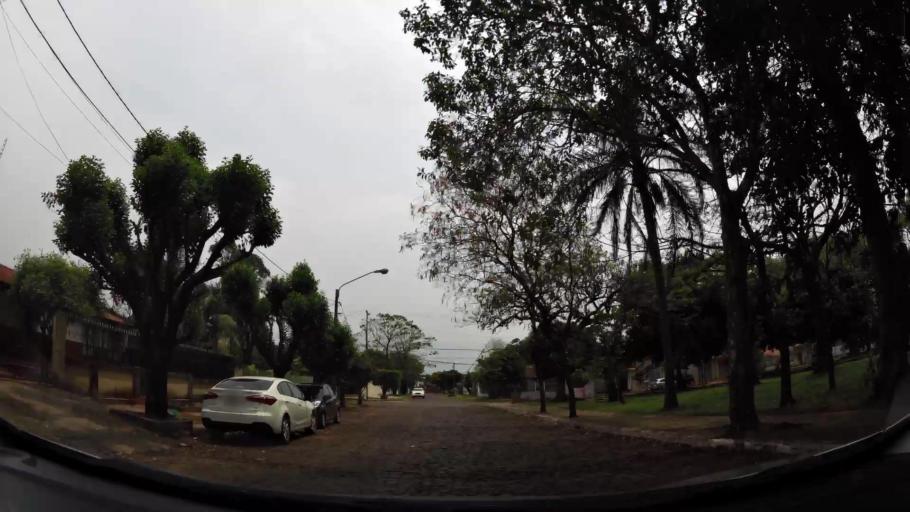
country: PY
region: Alto Parana
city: Presidente Franco
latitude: -25.5538
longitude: -54.6267
